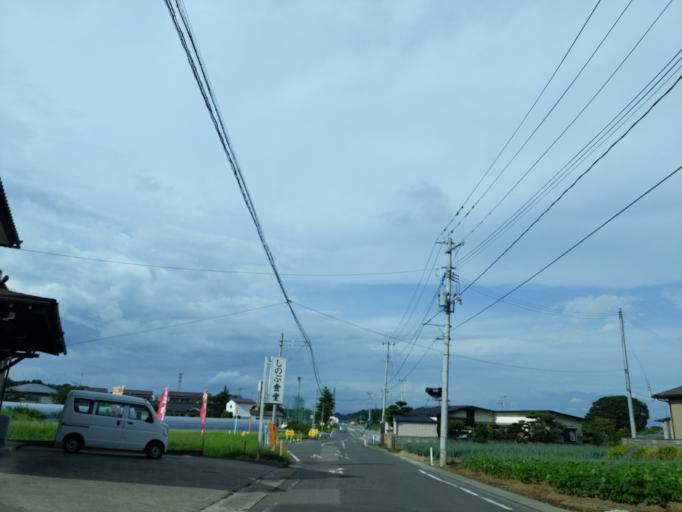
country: JP
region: Fukushima
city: Sukagawa
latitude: 37.3304
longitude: 140.3313
